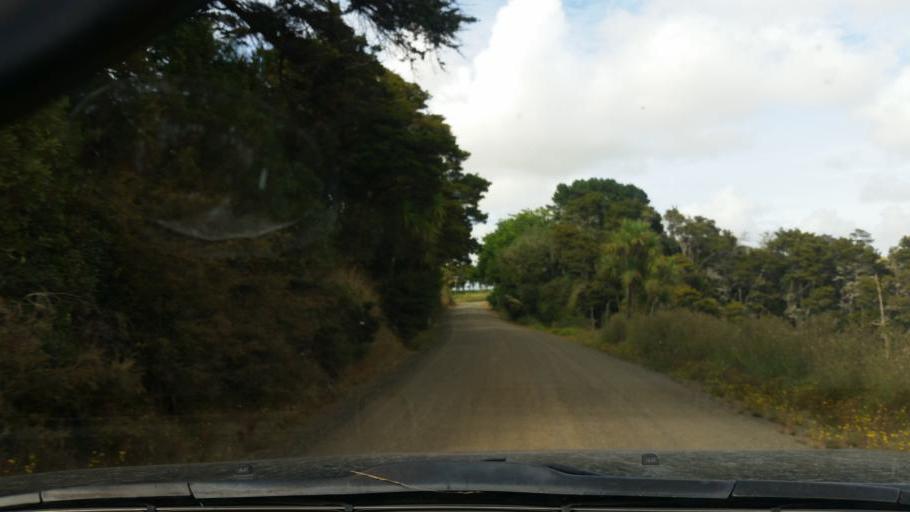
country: NZ
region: Northland
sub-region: Kaipara District
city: Dargaville
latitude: -35.9870
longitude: 173.9567
